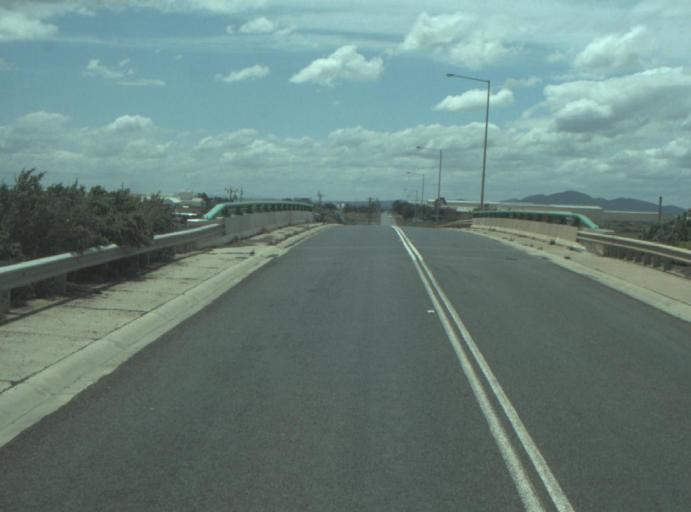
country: AU
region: Victoria
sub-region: Greater Geelong
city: Lara
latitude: -38.0597
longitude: 144.3782
